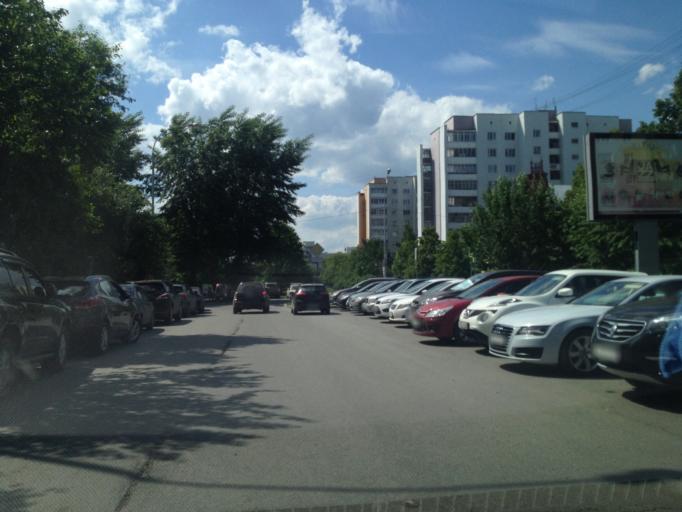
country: RU
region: Sverdlovsk
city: Yekaterinburg
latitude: 56.8388
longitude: 60.5888
